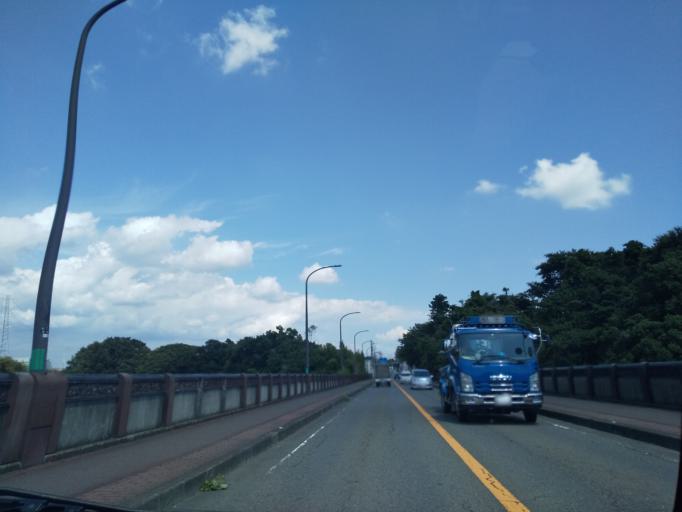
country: JP
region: Kanagawa
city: Zama
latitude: 35.4911
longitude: 139.4124
